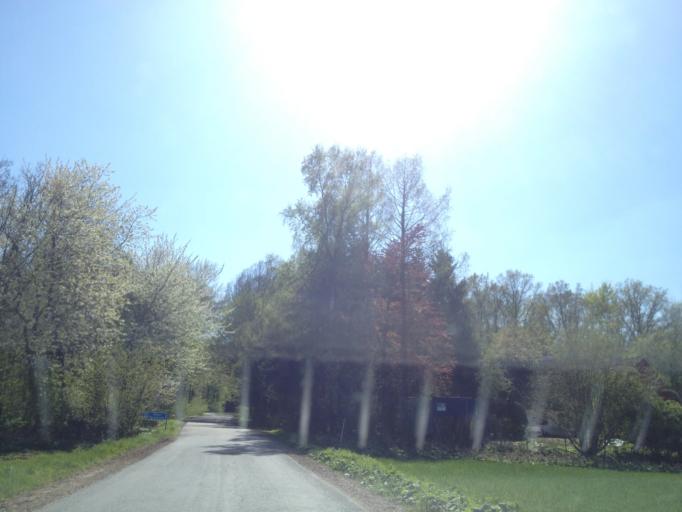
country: DK
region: Zealand
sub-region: Roskilde Kommune
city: Viby
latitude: 55.5288
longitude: 12.0166
